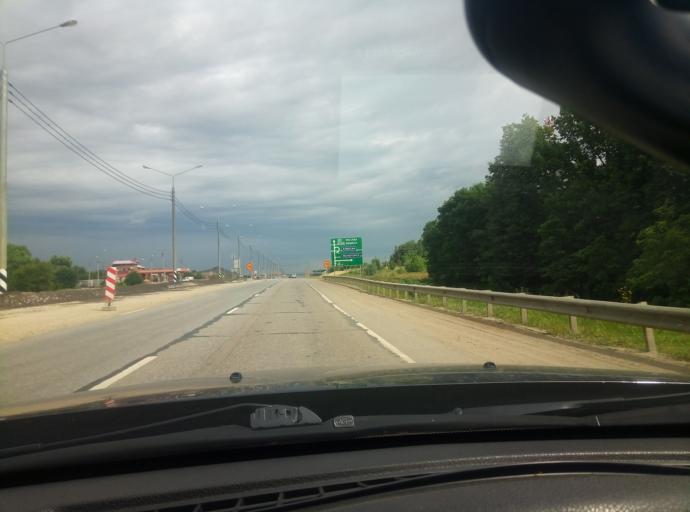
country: RU
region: Tula
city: Novogurovskiy
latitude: 54.4644
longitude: 37.5110
